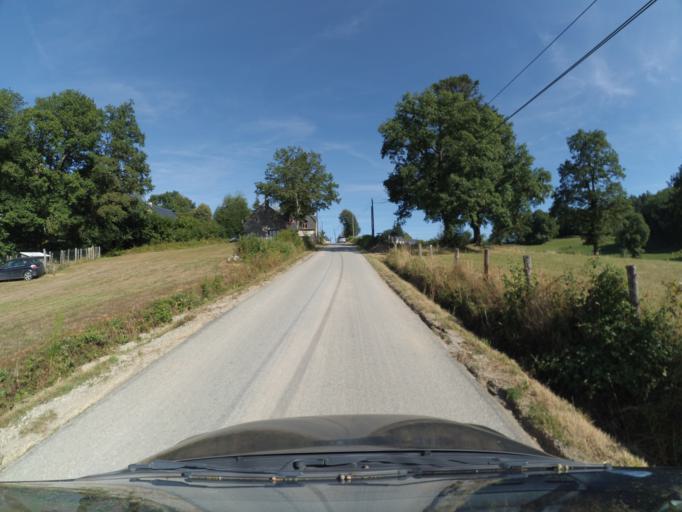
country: FR
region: Limousin
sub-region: Departement de la Correze
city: Bugeat
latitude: 45.7017
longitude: 1.8766
